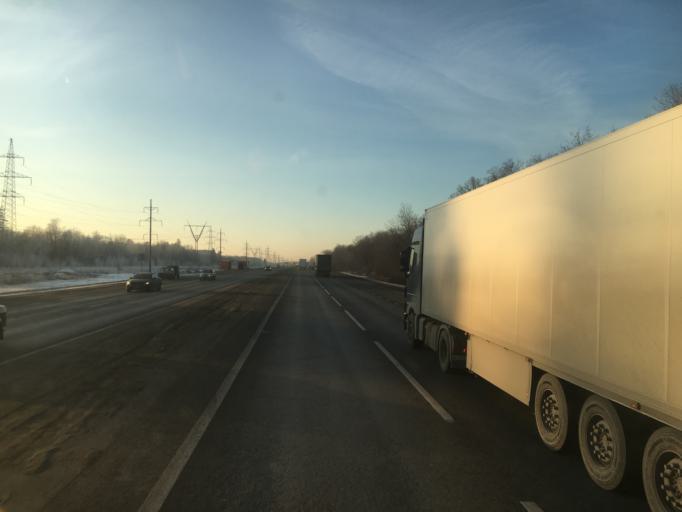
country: RU
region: Samara
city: Pribrezhnyy
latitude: 53.5166
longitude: 49.8541
